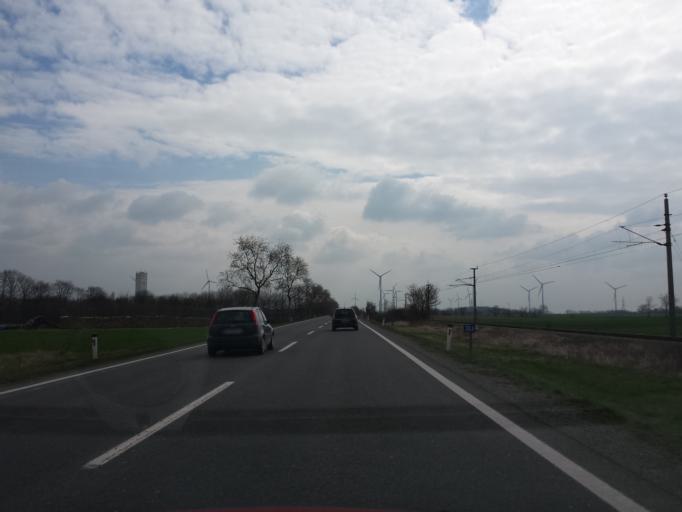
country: AT
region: Lower Austria
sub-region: Politischer Bezirk Bruck an der Leitha
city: Petronell-Carnuntum
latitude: 48.1075
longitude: 16.8534
